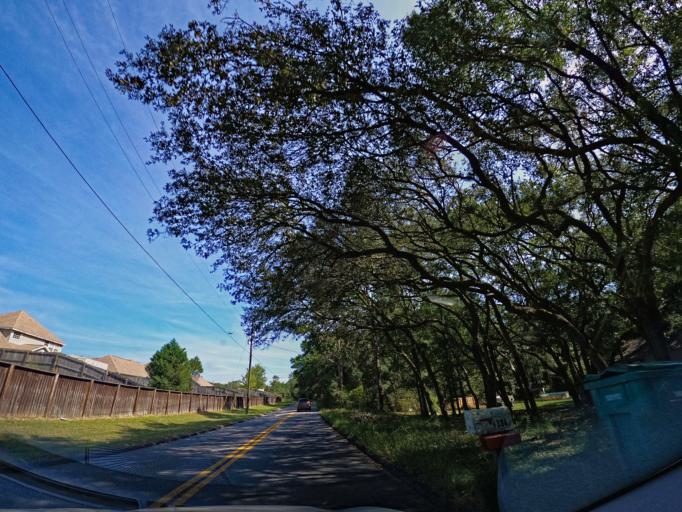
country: US
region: Florida
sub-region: Okaloosa County
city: Crestview
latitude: 30.7042
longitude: -86.5841
